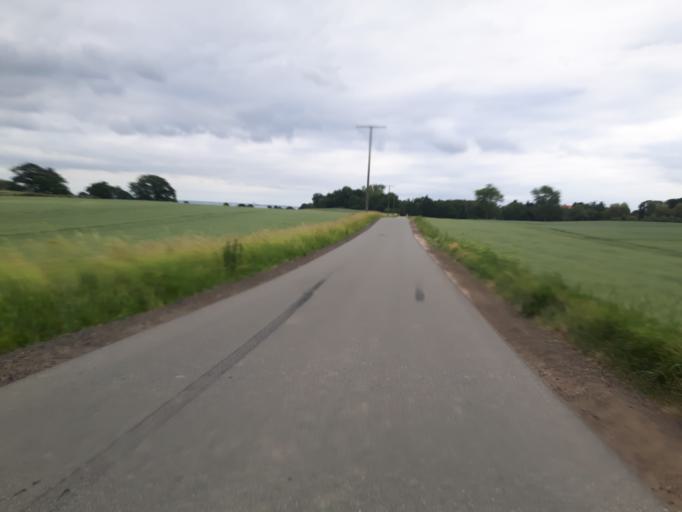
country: DE
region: Schleswig-Holstein
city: Schashagen
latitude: 54.1204
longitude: 10.9060
